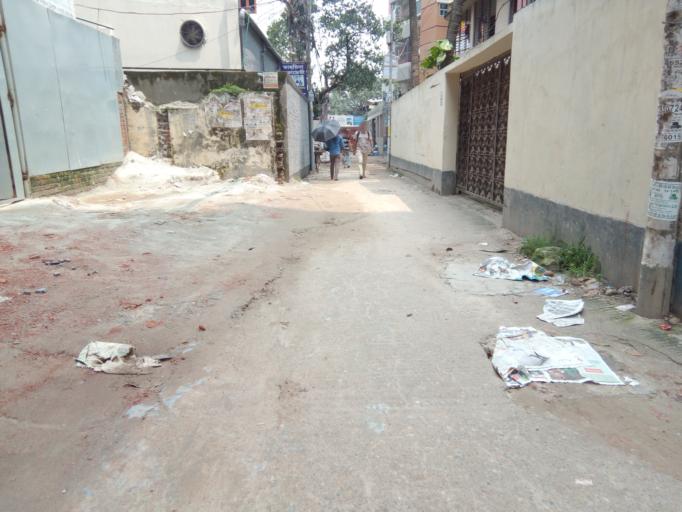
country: BD
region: Dhaka
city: Azimpur
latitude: 23.7369
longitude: 90.3885
